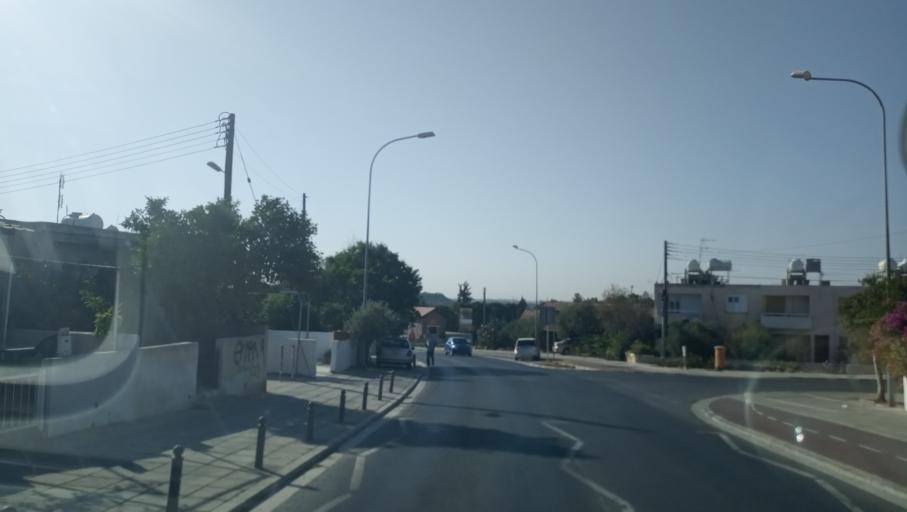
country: CY
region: Lefkosia
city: Geri
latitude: 35.1461
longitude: 33.4005
